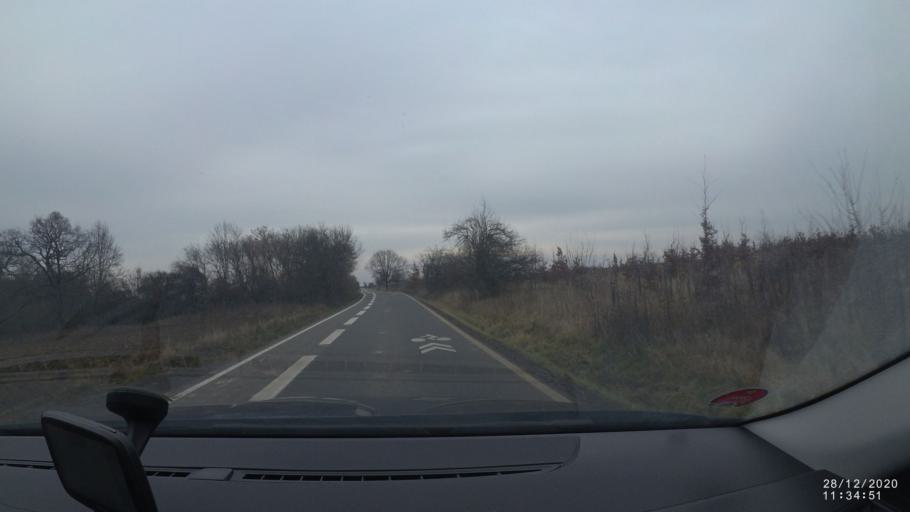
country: CZ
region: Praha
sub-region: Praha 19
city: Satalice
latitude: 50.1295
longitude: 14.5877
